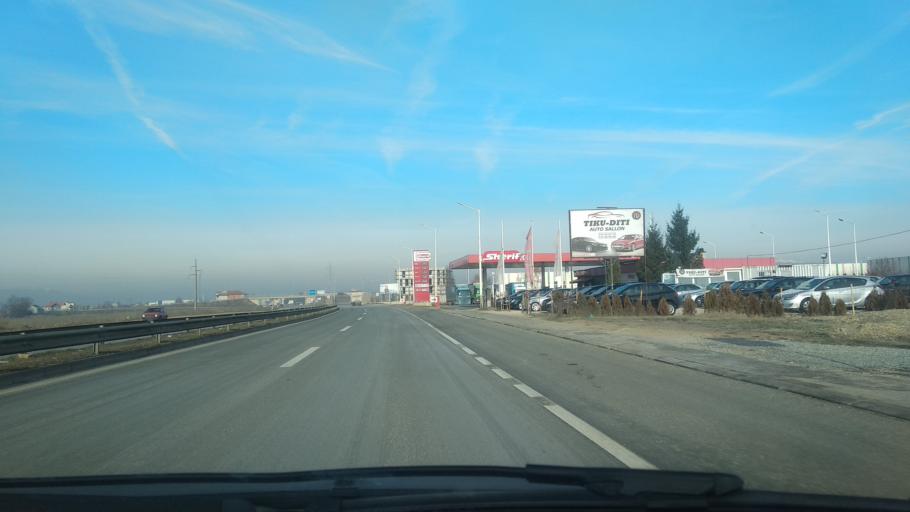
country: XK
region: Pristina
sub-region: Komuna e Obiliqit
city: Obiliq
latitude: 42.7146
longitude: 21.0975
